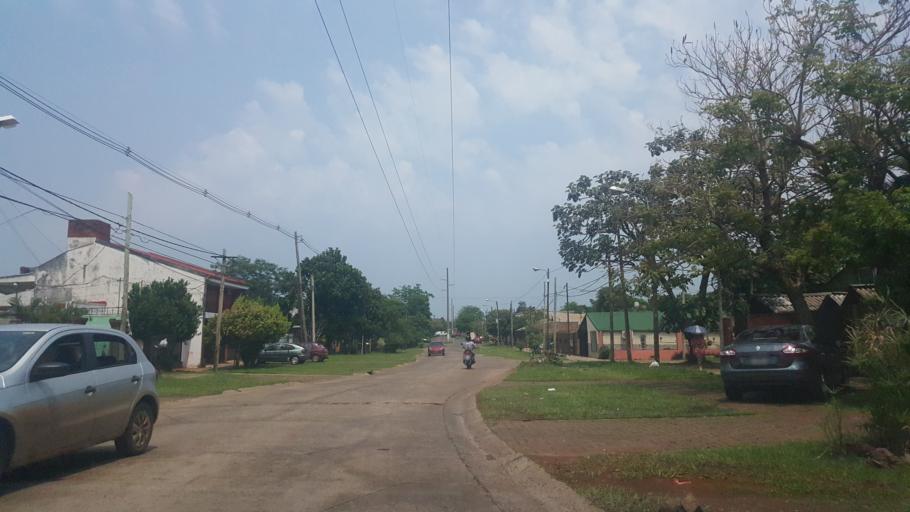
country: AR
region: Misiones
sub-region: Departamento de Capital
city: Posadas
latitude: -27.3665
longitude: -55.9126
